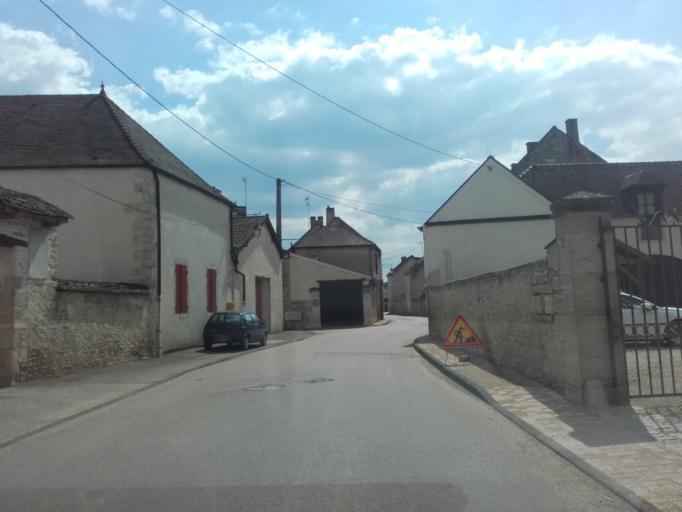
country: FR
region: Bourgogne
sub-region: Departement de la Cote-d'Or
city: Meursault
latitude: 46.9745
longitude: 4.7709
